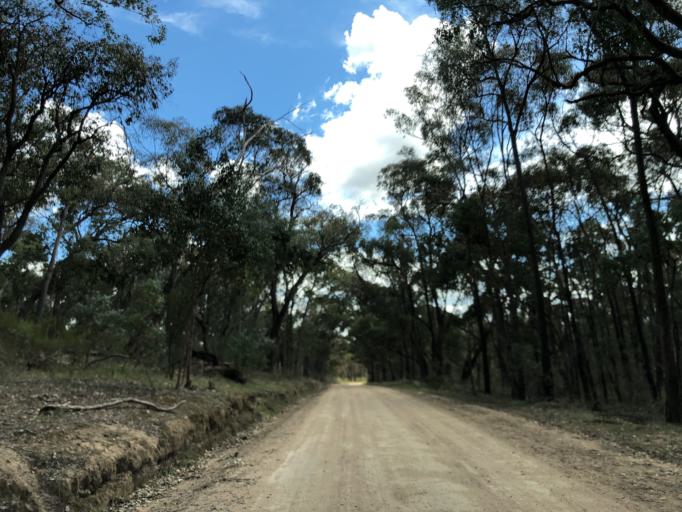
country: AU
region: Victoria
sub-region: Benalla
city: Benalla
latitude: -36.7392
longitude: 146.1538
